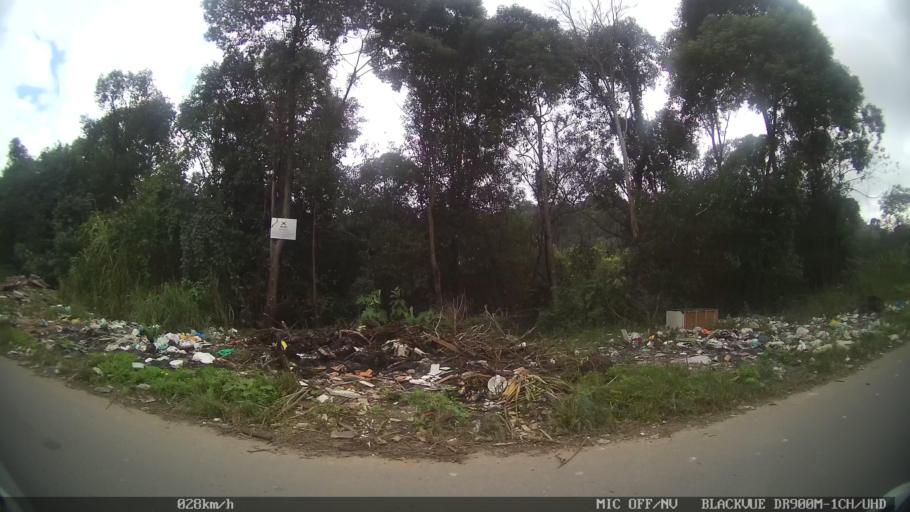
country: BR
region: Parana
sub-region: Colombo
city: Colombo
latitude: -25.3446
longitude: -49.2331
